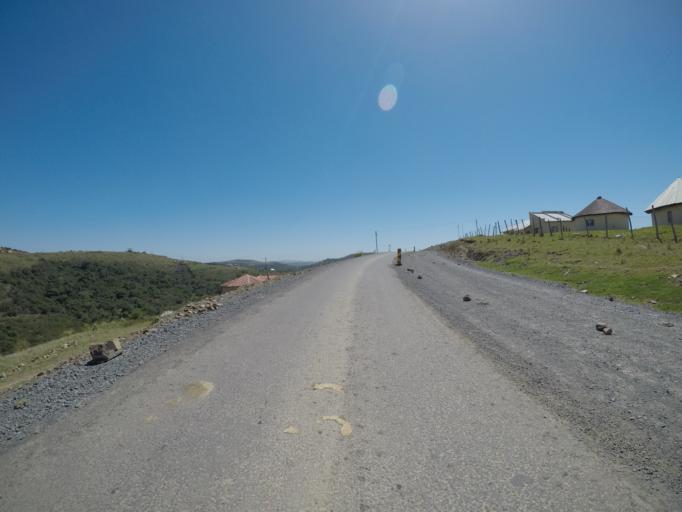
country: ZA
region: Eastern Cape
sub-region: OR Tambo District Municipality
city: Libode
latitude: -32.0041
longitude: 29.1156
